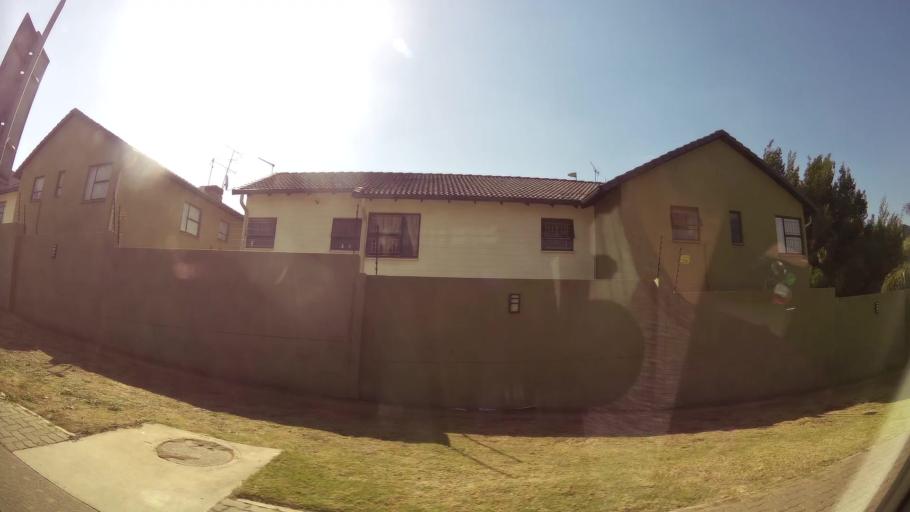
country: ZA
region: Gauteng
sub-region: City of Johannesburg Metropolitan Municipality
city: Johannesburg
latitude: -26.2705
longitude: 28.0429
